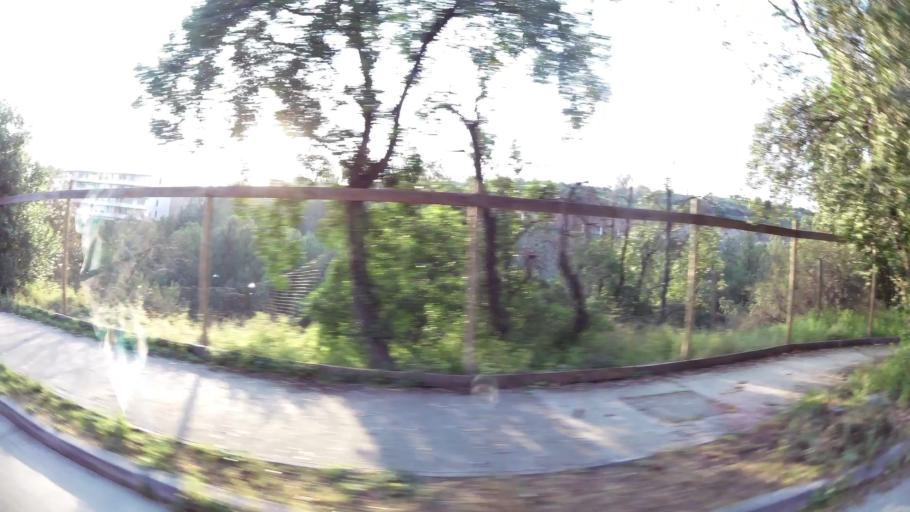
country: CL
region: Santiago Metropolitan
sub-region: Provincia de Santiago
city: Villa Presidente Frei, Nunoa, Santiago, Chile
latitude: -33.3307
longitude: -70.5081
